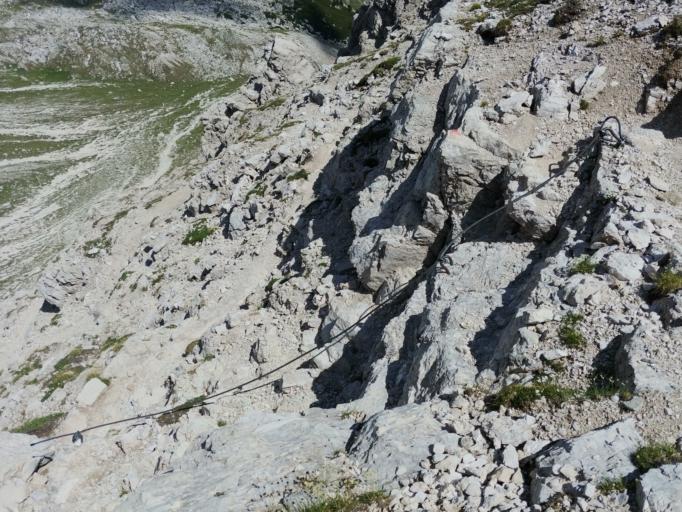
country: IT
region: Trentino-Alto Adige
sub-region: Bolzano
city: Selva
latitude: 46.5870
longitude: 11.7891
